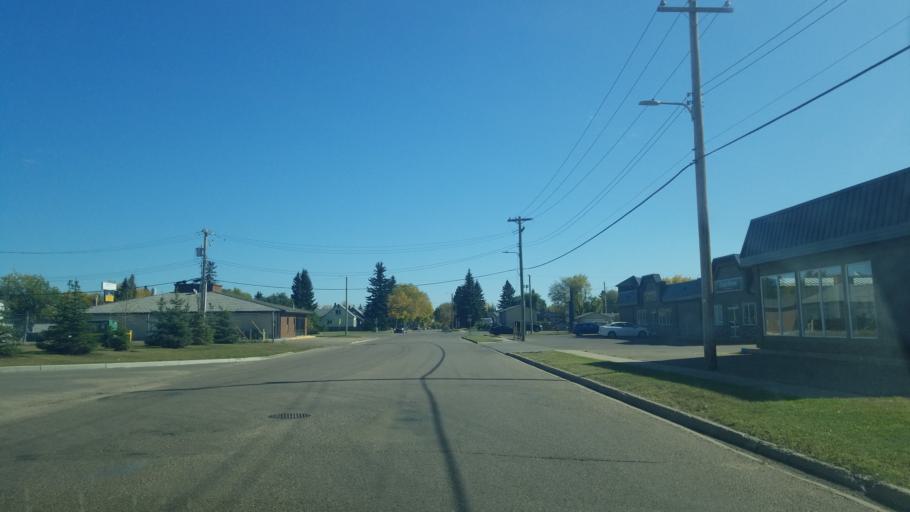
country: CA
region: Saskatchewan
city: Lloydminster
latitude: 53.2752
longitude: -110.0072
